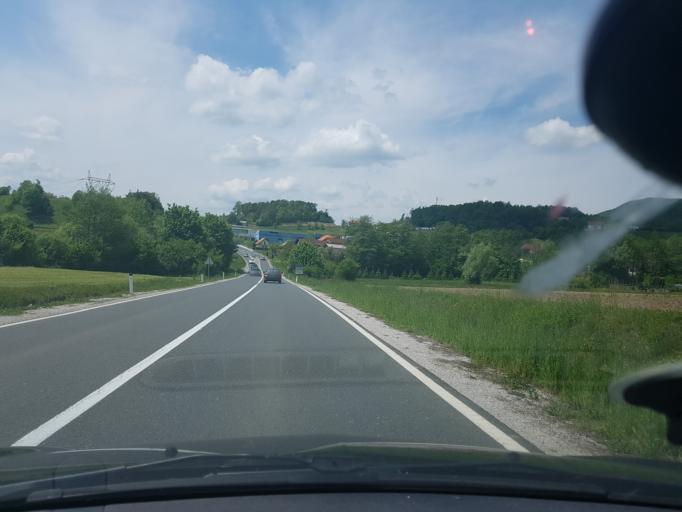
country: SI
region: Rogaska Slatina
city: Rogaska Slatina
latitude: 46.2530
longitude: 15.6238
